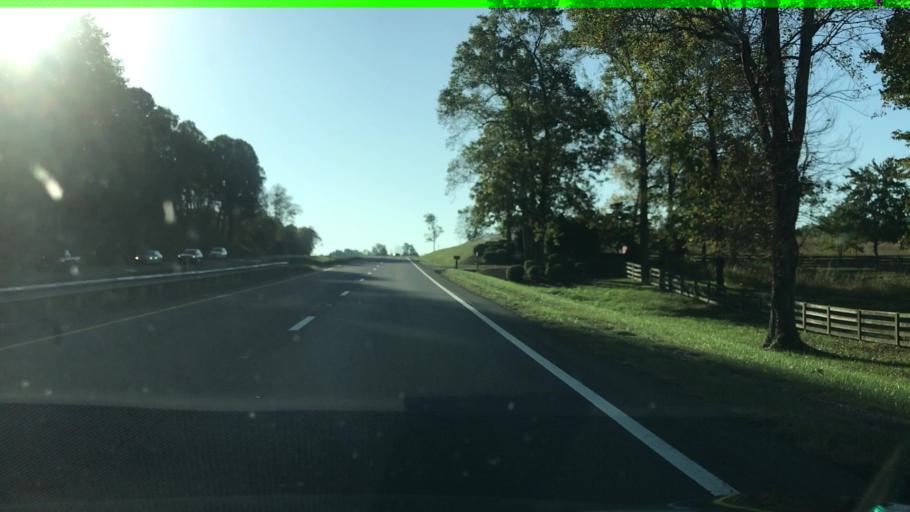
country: US
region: Virginia
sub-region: Bedford County
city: Forest
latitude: 37.3050
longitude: -79.3887
